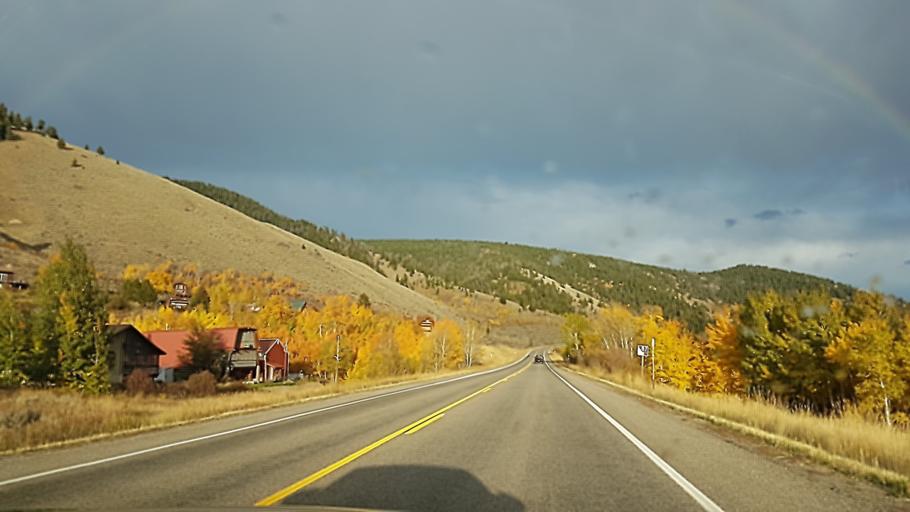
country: US
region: Montana
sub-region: Gallatin County
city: West Yellowstone
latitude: 44.6627
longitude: -111.3759
